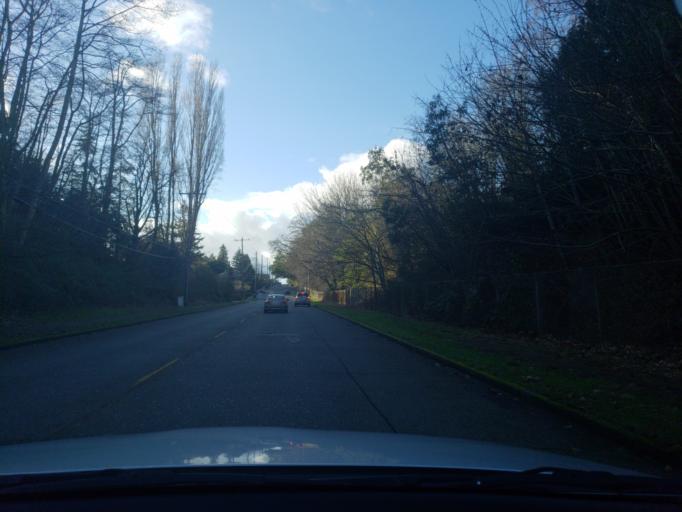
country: US
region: Washington
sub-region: King County
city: Seattle
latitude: 47.6541
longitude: -122.4053
